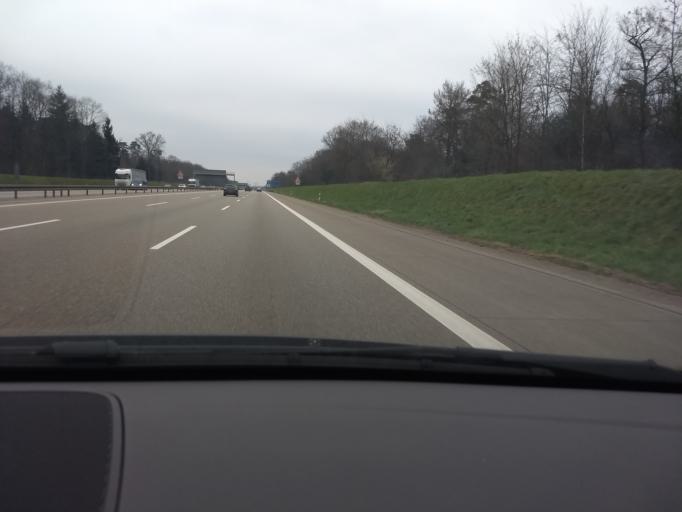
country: DE
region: Baden-Wuerttemberg
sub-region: Karlsruhe Region
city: Sinzheim
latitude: 48.7989
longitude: 8.1695
